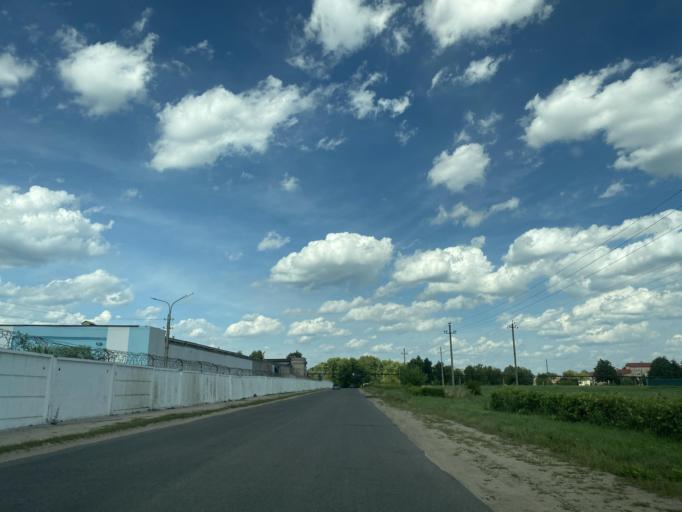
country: BY
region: Minsk
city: Horad Zhodzina
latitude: 54.0928
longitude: 28.3530
